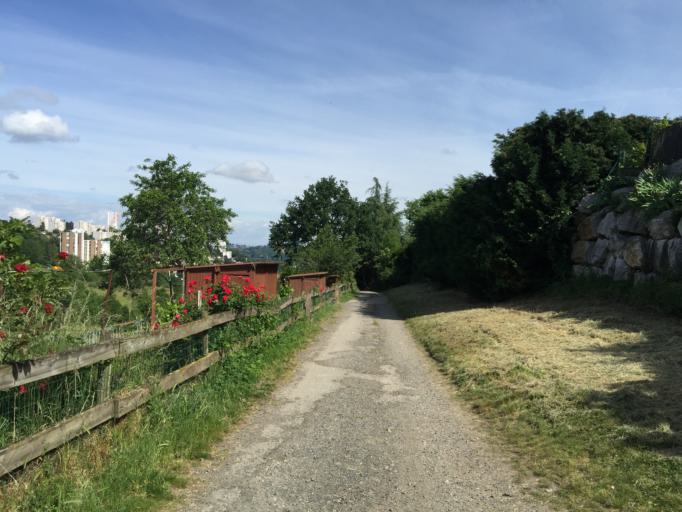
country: FR
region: Rhone-Alpes
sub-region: Departement de la Loire
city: Saint-Priest-en-Jarez
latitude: 45.4585
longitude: 4.3740
